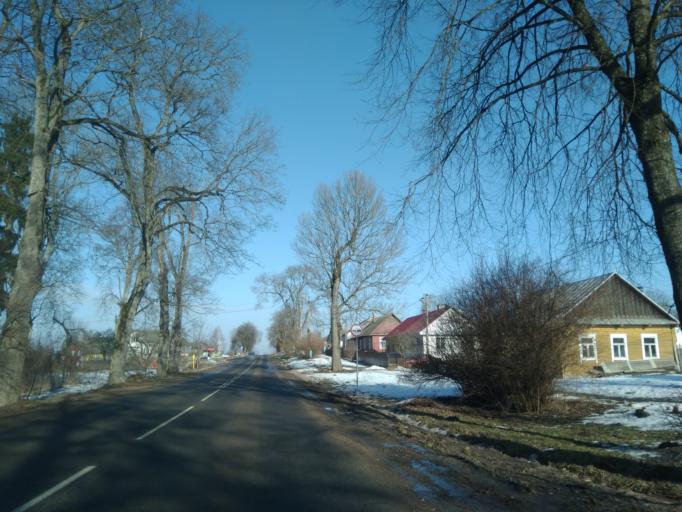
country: BY
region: Minsk
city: Nyasvizh
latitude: 53.2054
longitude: 26.6598
